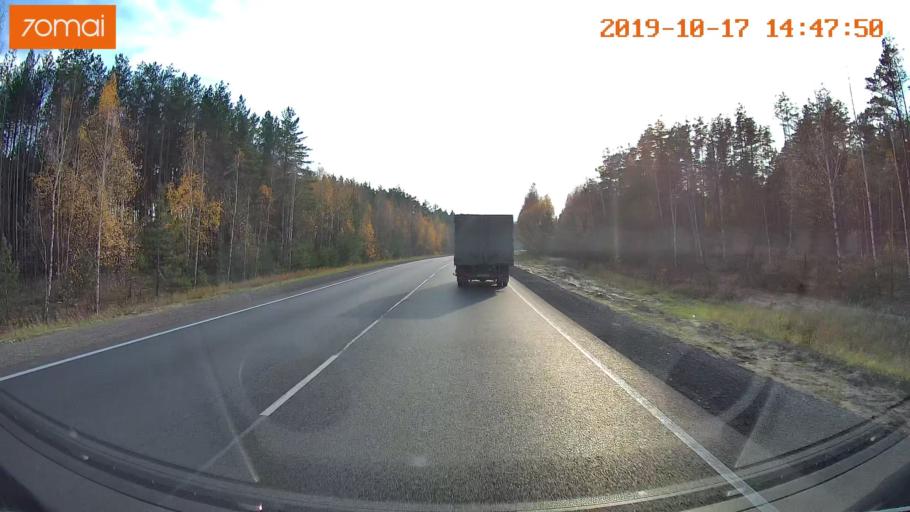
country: RU
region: Rjazan
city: Solotcha
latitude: 54.7660
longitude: 39.8568
